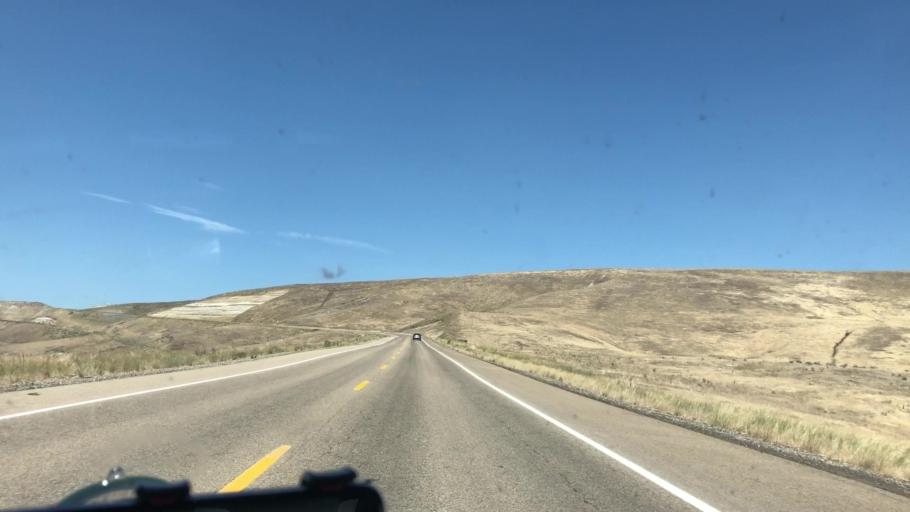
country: US
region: Idaho
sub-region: Owyhee County
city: Marsing
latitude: 43.2835
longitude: -116.9900
